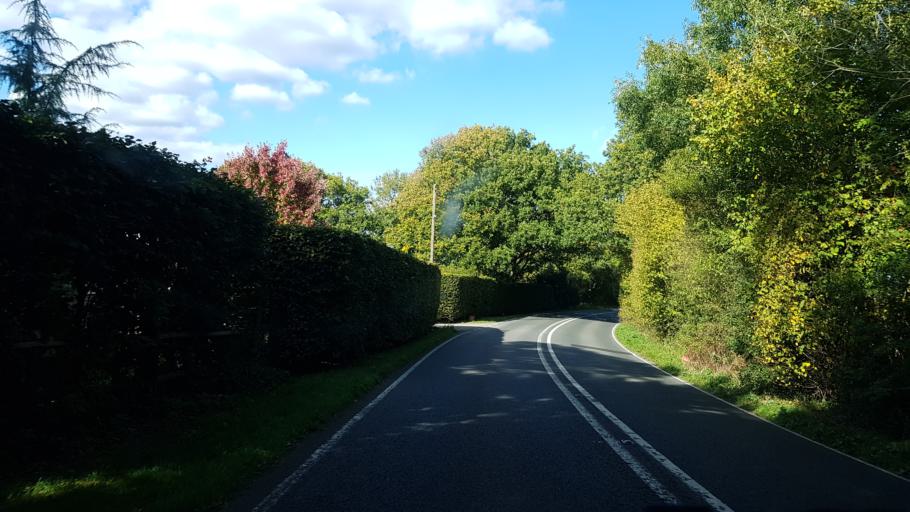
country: GB
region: England
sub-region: Surrey
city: Chiddingfold
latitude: 51.0652
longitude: -0.6441
